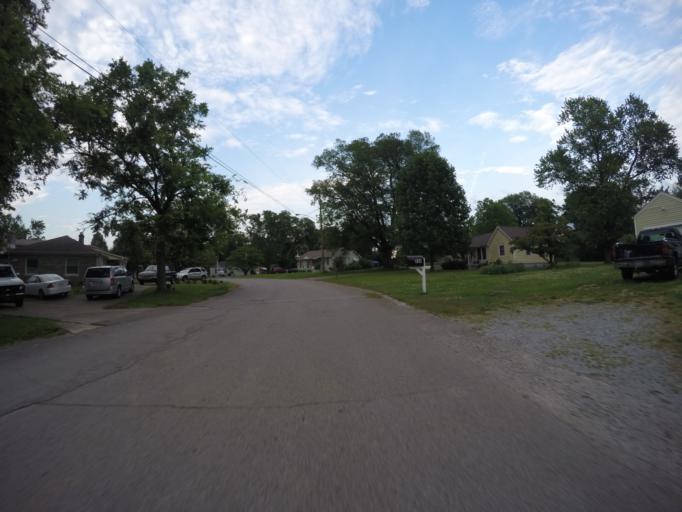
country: US
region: Tennessee
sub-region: Davidson County
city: Lakewood
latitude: 36.2410
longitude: -86.6296
